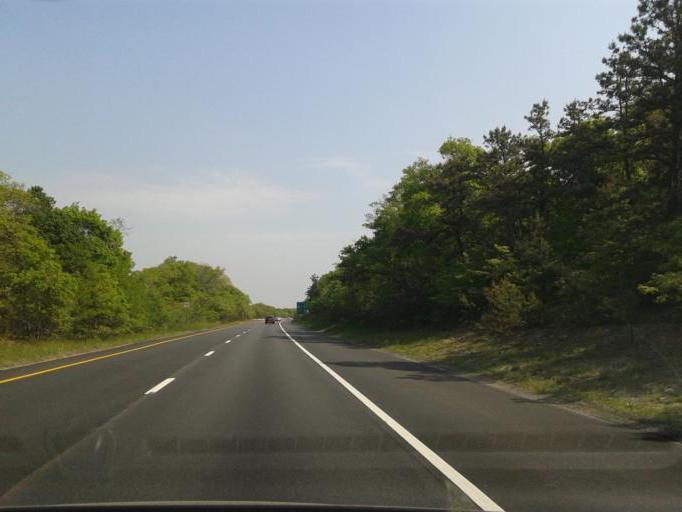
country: US
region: Massachusetts
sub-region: Barnstable County
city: Pocasset
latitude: 41.6735
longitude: -70.5970
